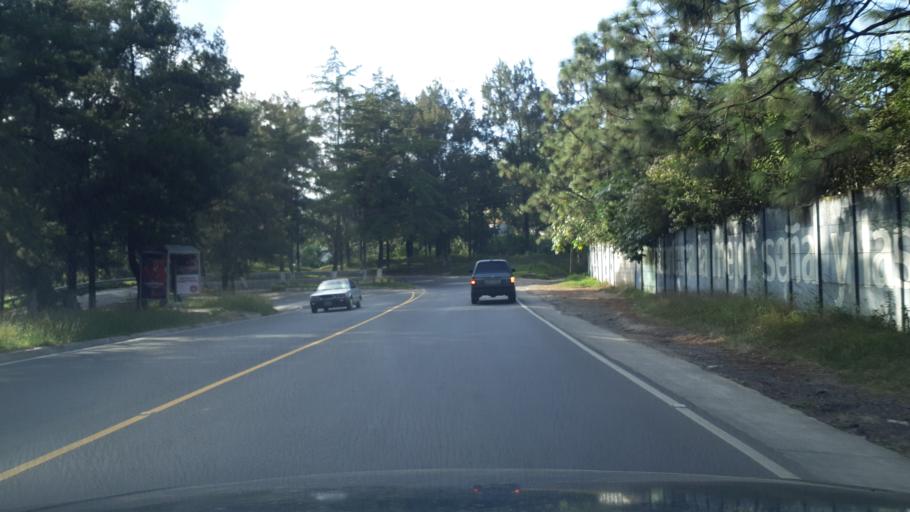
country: GT
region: Chimaltenango
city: El Tejar
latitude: 14.6378
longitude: -90.8128
